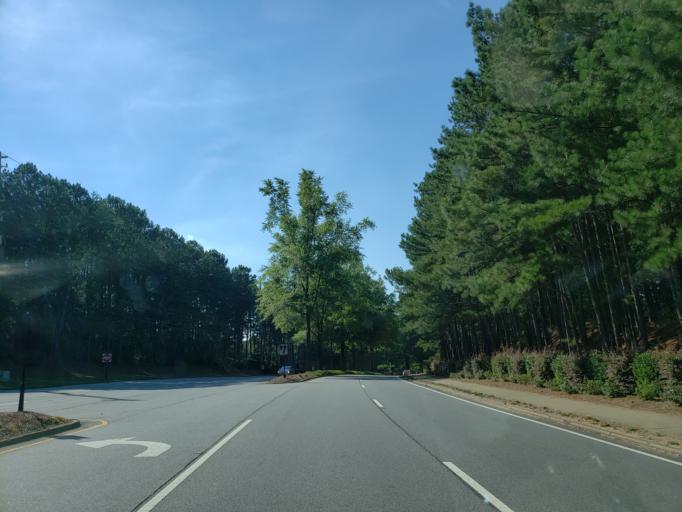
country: US
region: Georgia
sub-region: Cherokee County
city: Woodstock
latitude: 34.1231
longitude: -84.5576
